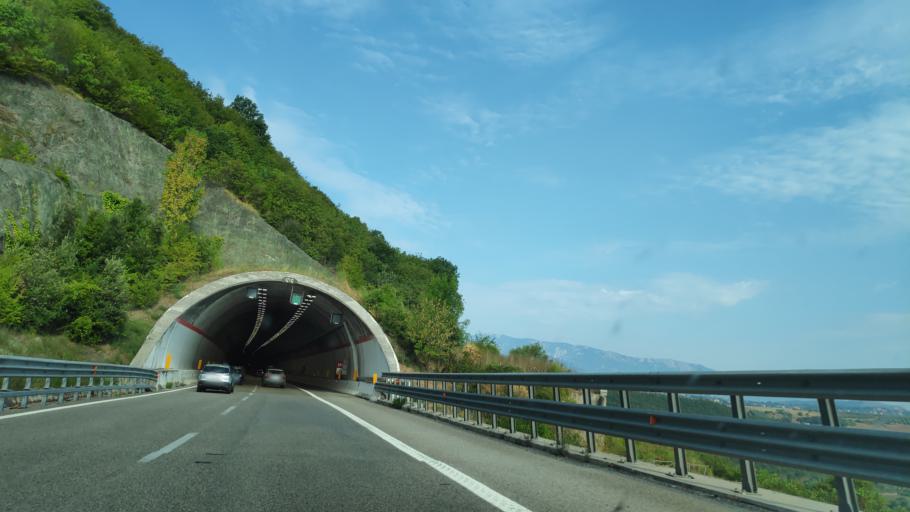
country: IT
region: Campania
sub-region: Provincia di Salerno
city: Sicignano degli Alburni
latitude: 40.6003
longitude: 15.3107
